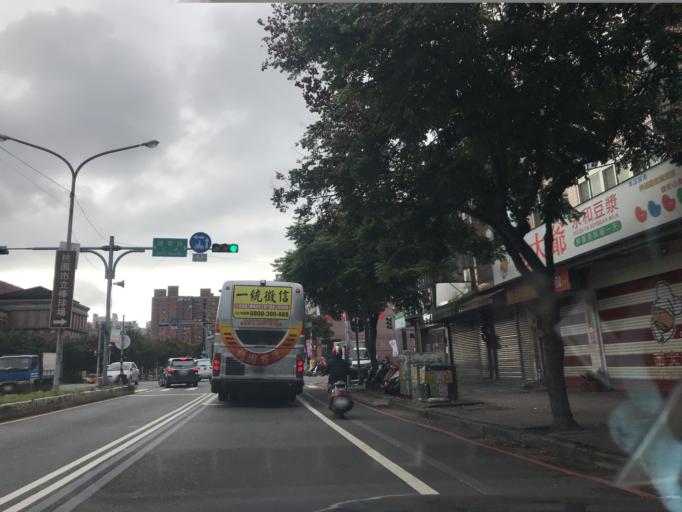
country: TW
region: Taiwan
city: Daxi
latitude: 24.9401
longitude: 121.2193
